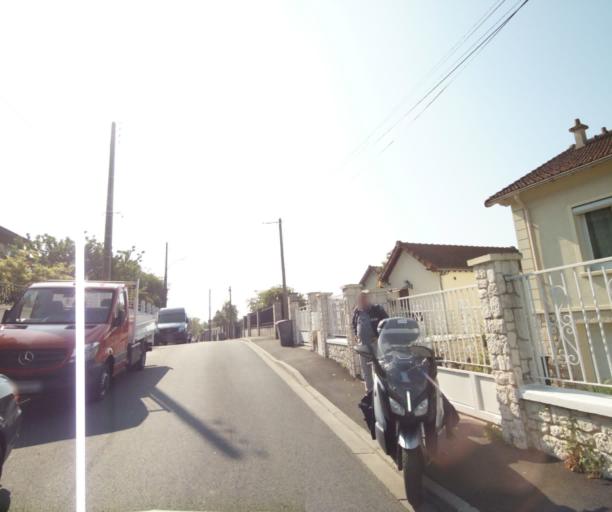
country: FR
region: Ile-de-France
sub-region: Departement du Val-d'Oise
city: Sannois
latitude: 48.9666
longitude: 2.2426
